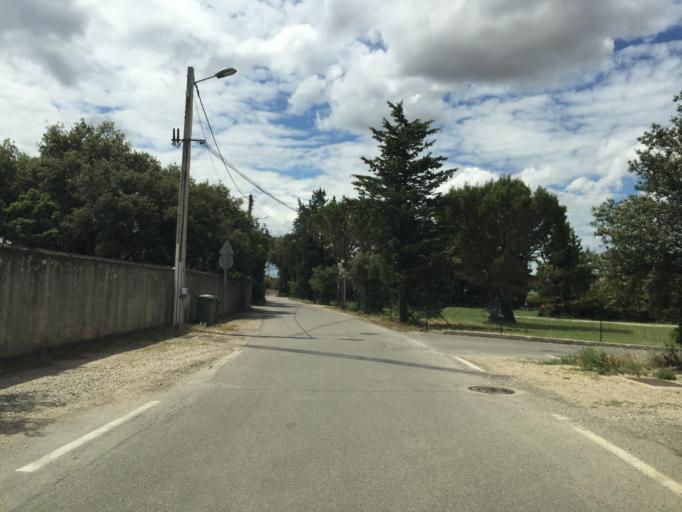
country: FR
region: Provence-Alpes-Cote d'Azur
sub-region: Departement du Vaucluse
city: Sorgues
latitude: 44.0197
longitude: 4.8617
